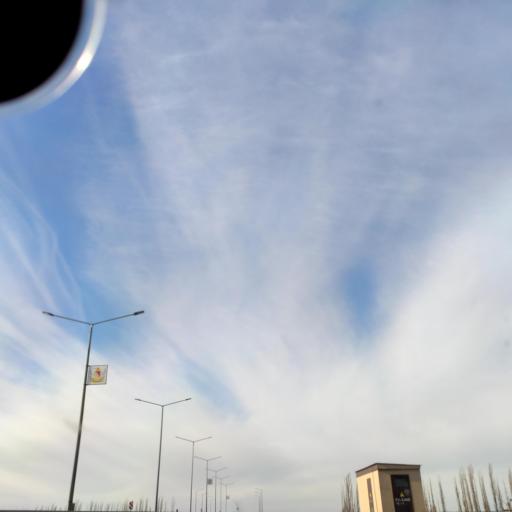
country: RU
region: Voronezj
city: Kashirskoye
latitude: 51.4808
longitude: 39.5472
